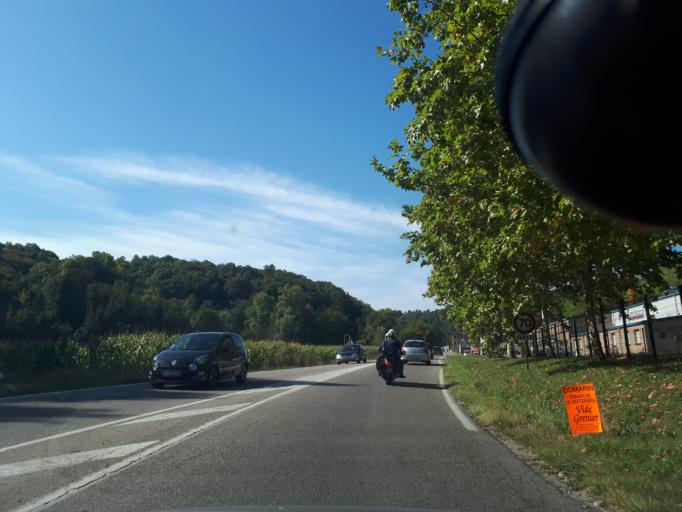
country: FR
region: Rhone-Alpes
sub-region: Departement de l'Isere
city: Maubec
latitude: 45.5668
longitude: 5.2808
